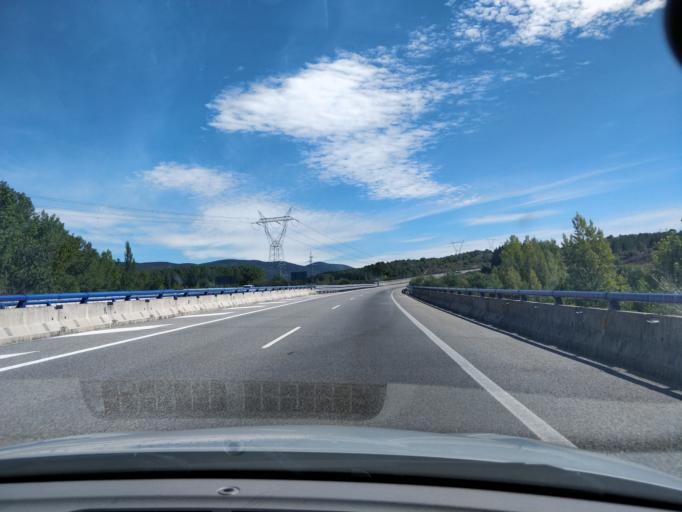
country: ES
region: Castille and Leon
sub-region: Provincia de Leon
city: Bembibre
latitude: 42.6269
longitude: -6.4288
